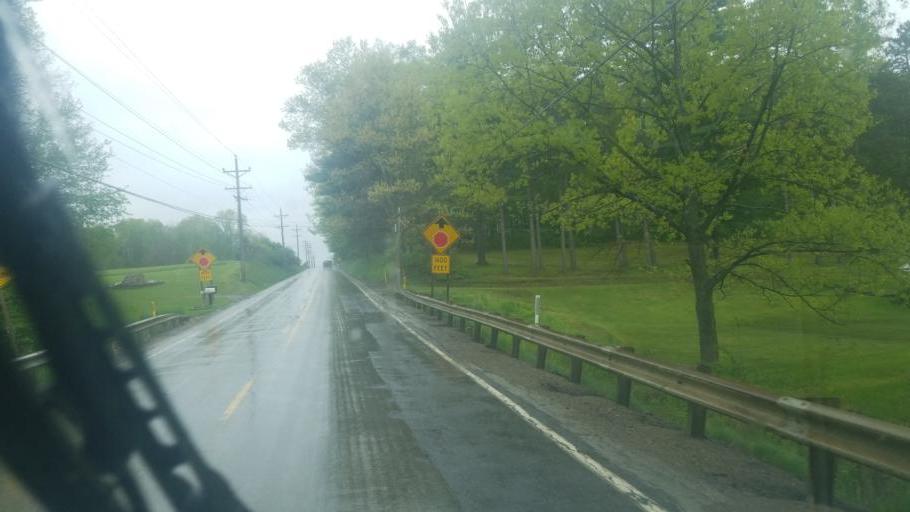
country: US
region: Pennsylvania
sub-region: Forest County
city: Tionesta
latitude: 41.3954
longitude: -79.3621
